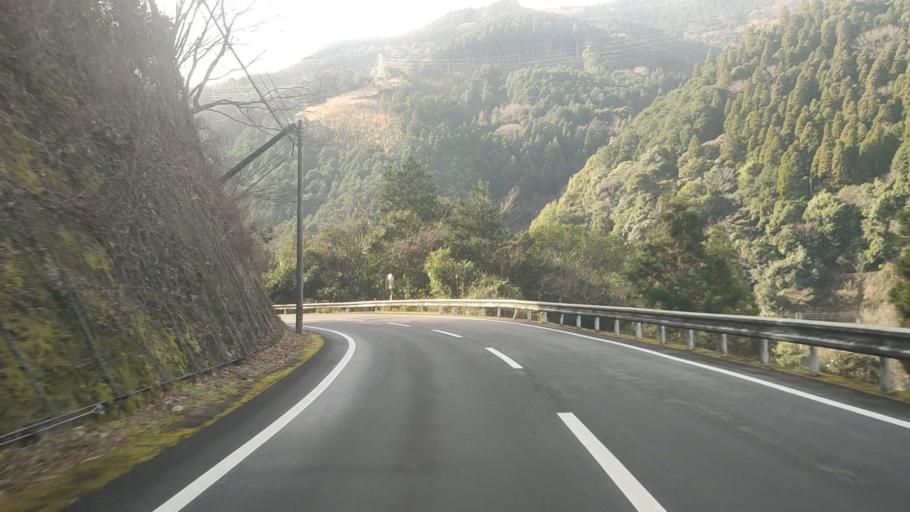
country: JP
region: Kumamoto
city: Hitoyoshi
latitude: 32.3225
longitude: 130.8398
